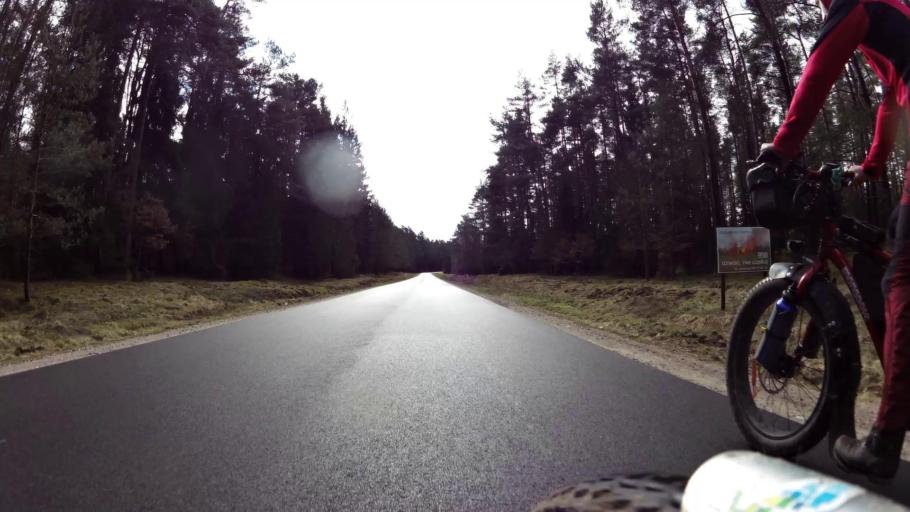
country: PL
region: Pomeranian Voivodeship
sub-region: Powiat bytowski
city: Kolczyglowy
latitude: 54.2052
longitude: 17.2351
